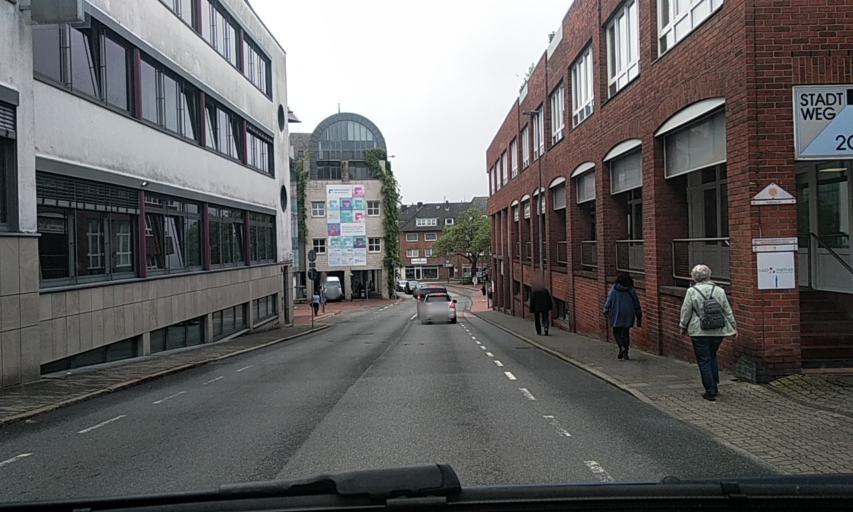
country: DE
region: Schleswig-Holstein
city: Schleswig
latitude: 54.5174
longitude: 9.5650
